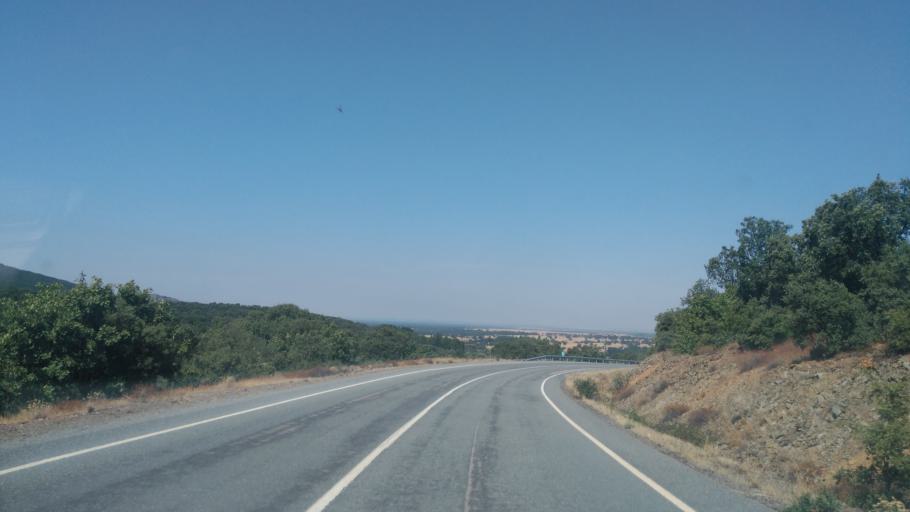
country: ES
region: Castille and Leon
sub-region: Provincia de Salamanca
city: Aldeanueva de la Sierra
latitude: 40.6046
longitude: -6.0934
